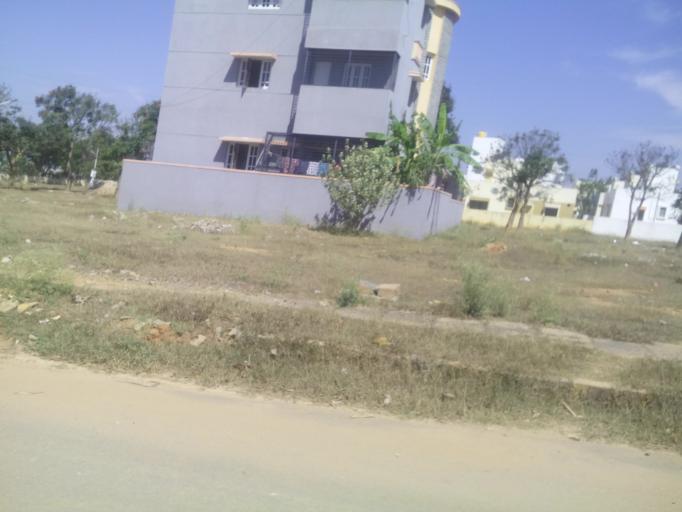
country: IN
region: Karnataka
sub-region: Bangalore Urban
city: Anekal
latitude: 12.7899
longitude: 77.7023
